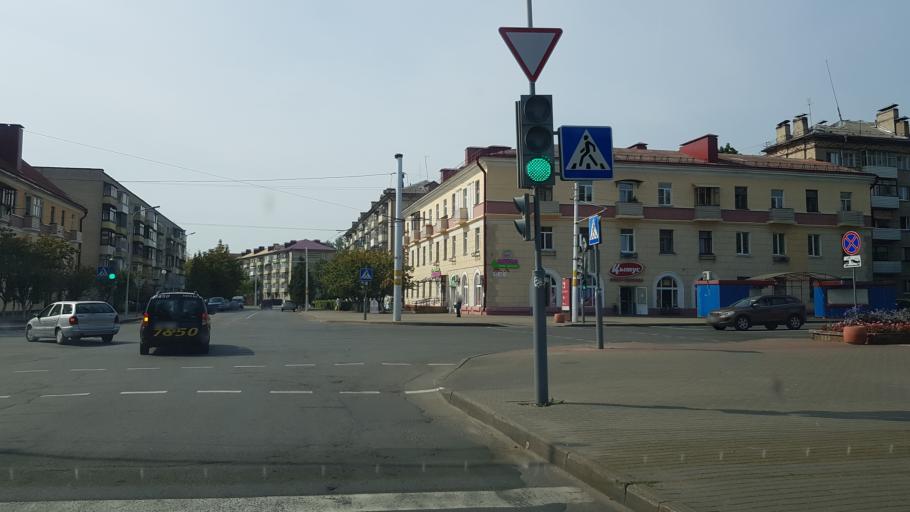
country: BY
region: Mogilev
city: Babruysk
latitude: 53.1473
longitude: 29.2328
